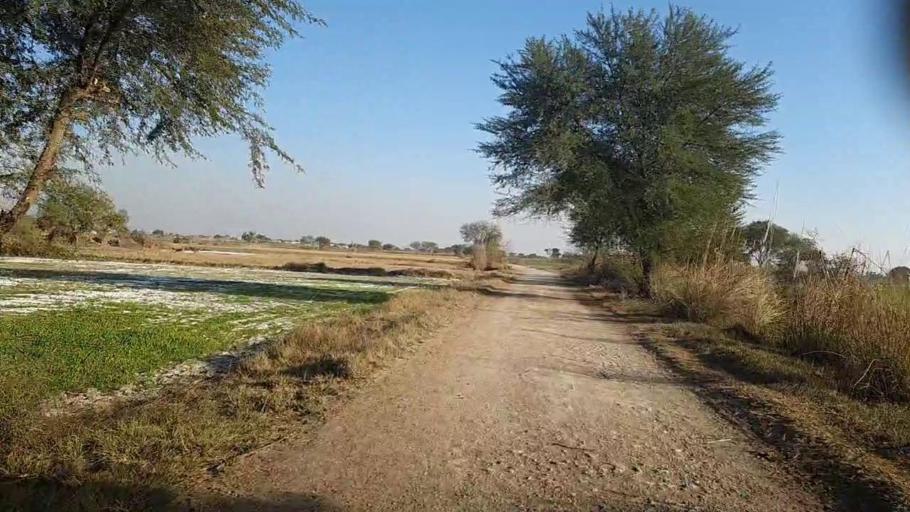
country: PK
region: Sindh
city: Khairpur
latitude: 27.9162
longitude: 69.7266
